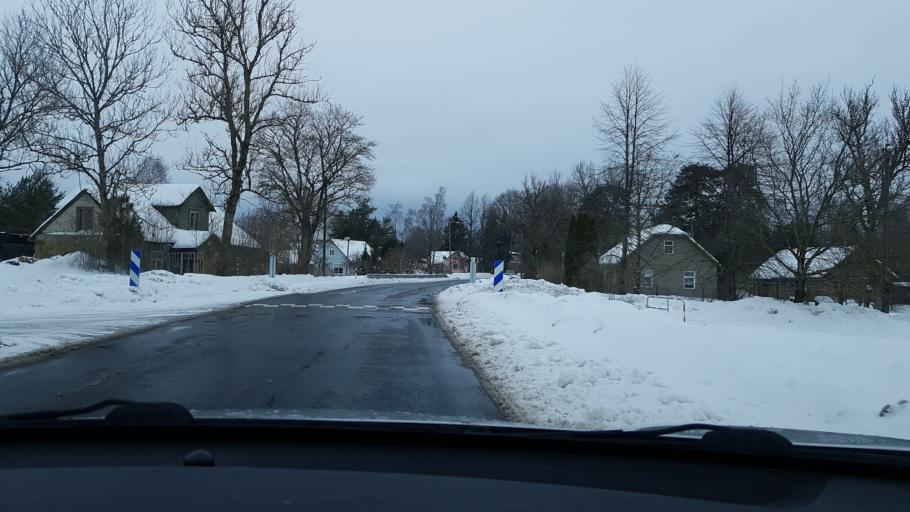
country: EE
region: Jaervamaa
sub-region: Jaerva-Jaani vald
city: Jarva-Jaani
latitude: 59.1406
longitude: 25.7533
